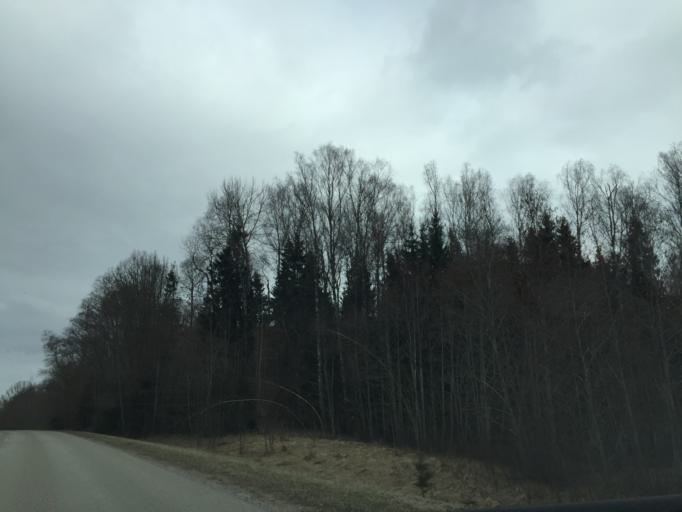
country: LV
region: Kraslavas Rajons
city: Kraslava
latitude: 55.9493
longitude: 27.1631
